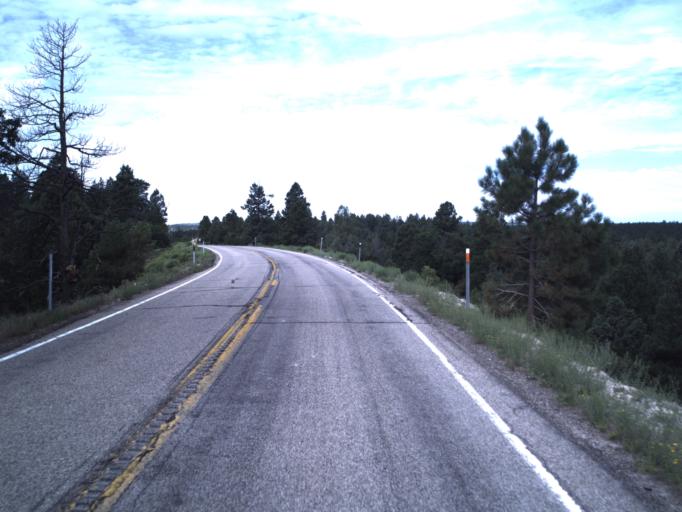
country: US
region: Utah
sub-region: Garfield County
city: Panguitch
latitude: 37.4969
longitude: -112.5470
